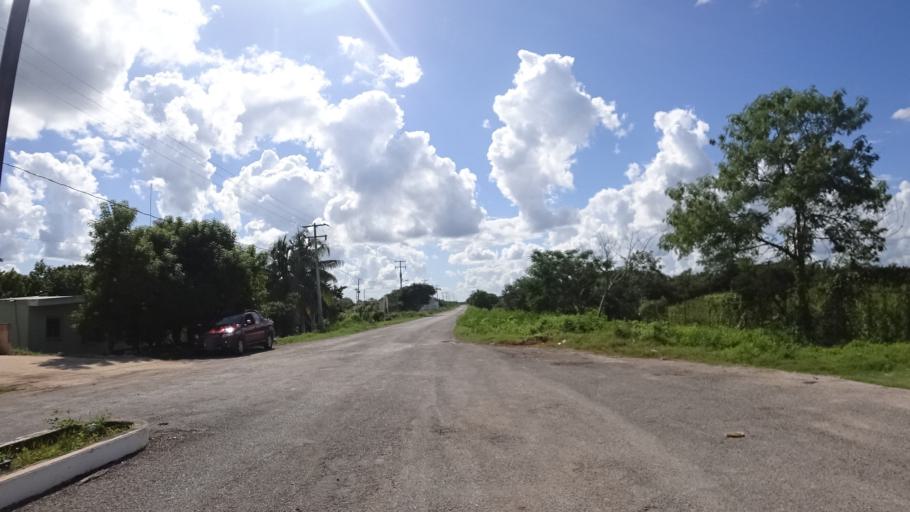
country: MX
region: Yucatan
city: Muna
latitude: 20.6471
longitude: -89.6897
